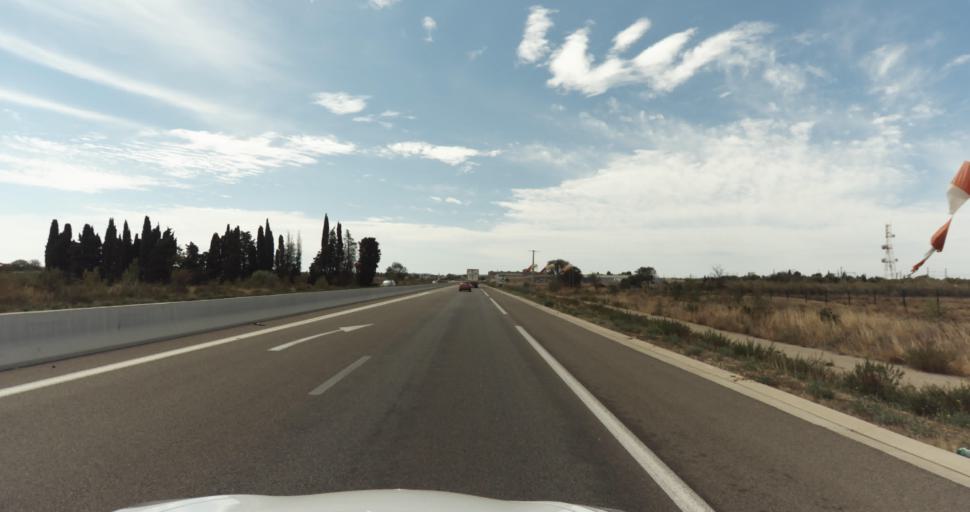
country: FR
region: Provence-Alpes-Cote d'Azur
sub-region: Departement des Bouches-du-Rhone
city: Miramas
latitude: 43.5914
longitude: 4.9892
